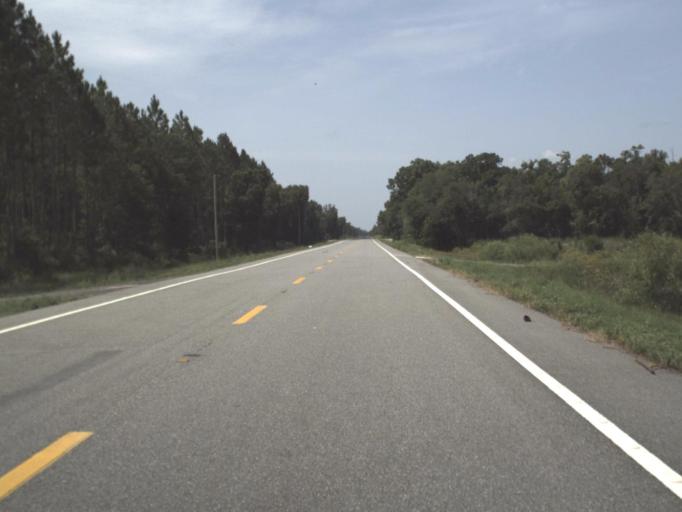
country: US
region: Florida
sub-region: Taylor County
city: Steinhatchee
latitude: 29.8132
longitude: -83.3173
